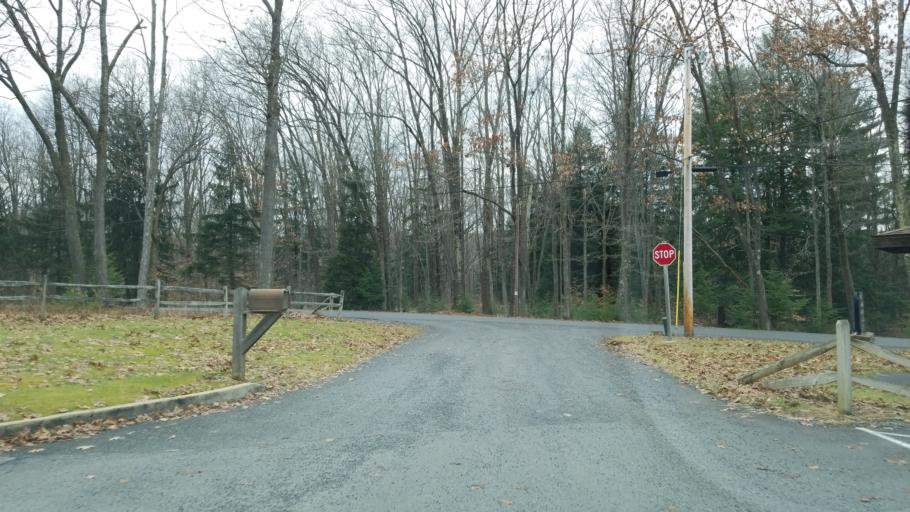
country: US
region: Pennsylvania
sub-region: Clearfield County
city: Clearfield
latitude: 41.1937
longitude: -78.5117
